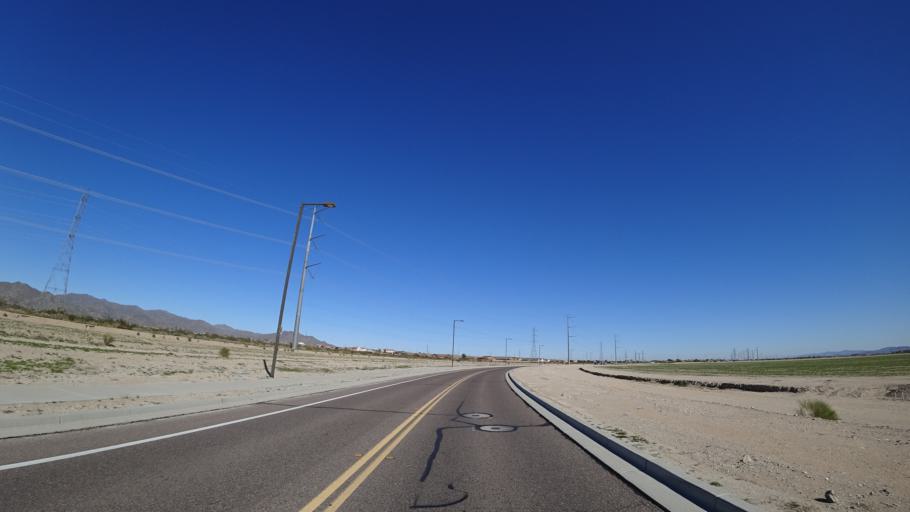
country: US
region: Arizona
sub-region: Maricopa County
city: Buckeye
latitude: 33.4210
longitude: -112.5679
